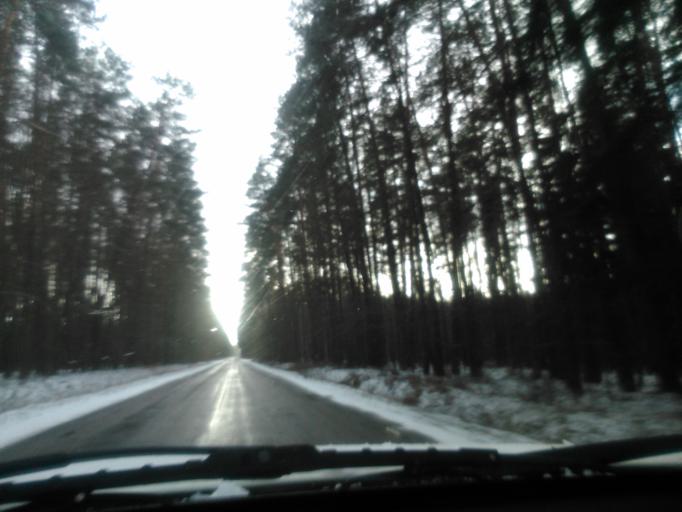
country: PL
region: Kujawsko-Pomorskie
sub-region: Powiat wabrzeski
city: Debowa Laka
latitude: 53.1820
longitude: 19.1461
